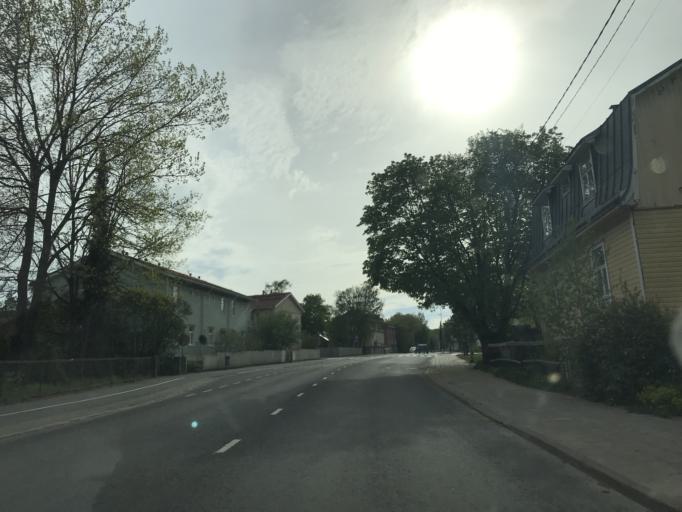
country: FI
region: Varsinais-Suomi
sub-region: Turku
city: Turku
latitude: 60.4559
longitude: 22.3114
